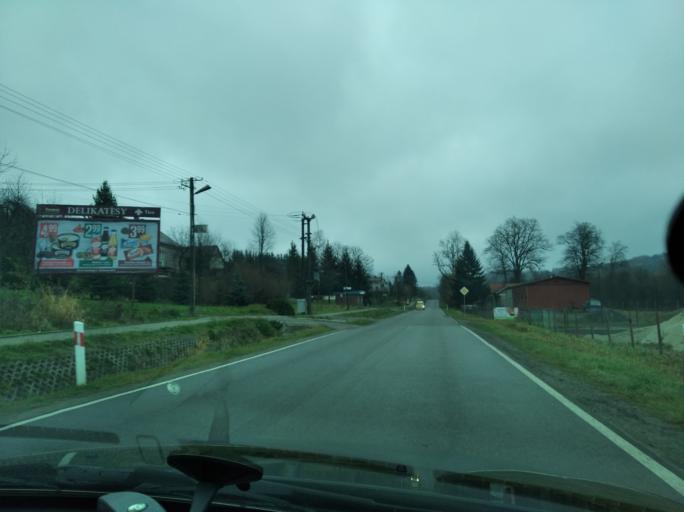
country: PL
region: Subcarpathian Voivodeship
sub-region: Powiat przeworski
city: Jawornik Polski
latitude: 49.8893
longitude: 22.2733
